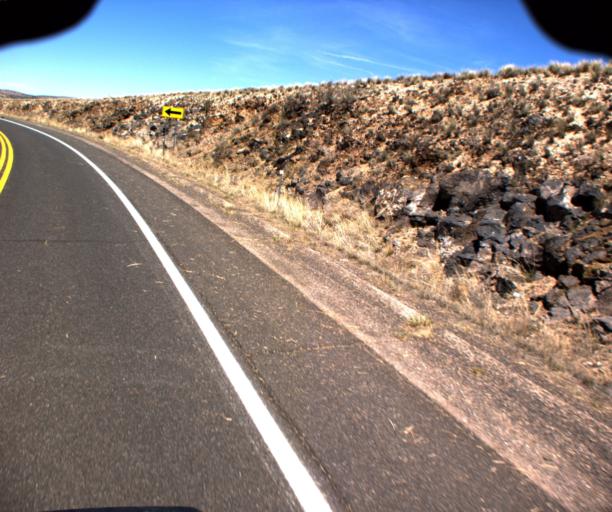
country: US
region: Arizona
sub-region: Yavapai County
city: Paulden
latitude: 35.3205
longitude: -112.8493
